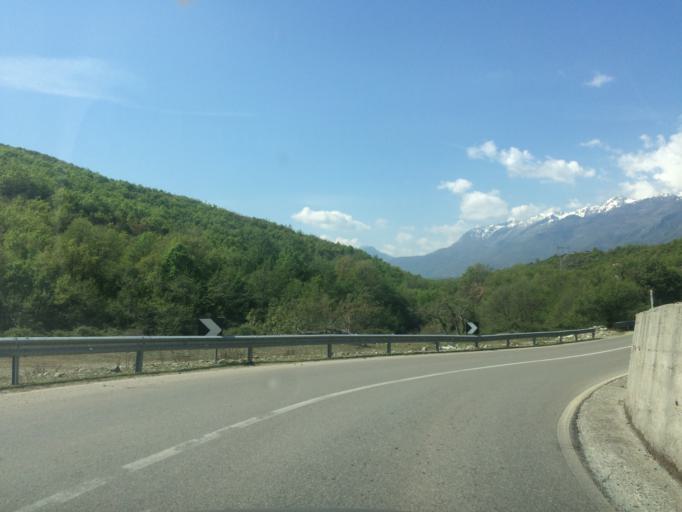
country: AL
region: Kukes
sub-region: Rrethi i Tropojes
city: Llugaj
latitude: 42.3837
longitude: 20.1385
